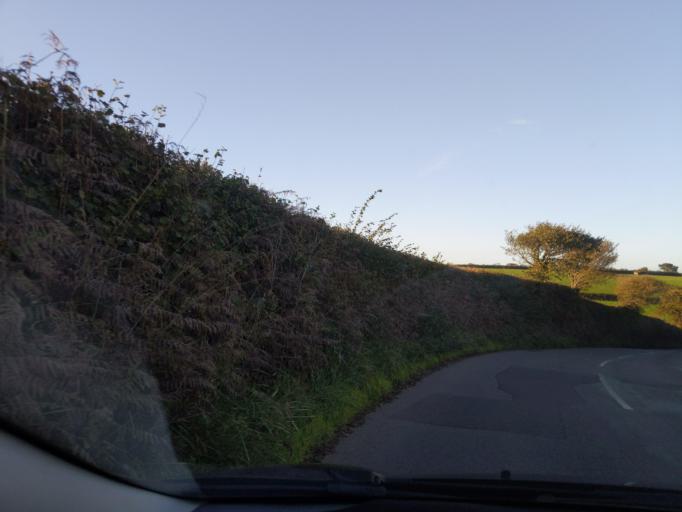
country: GB
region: England
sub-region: Plymouth
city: Plymstock
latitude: 50.3381
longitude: -4.0963
